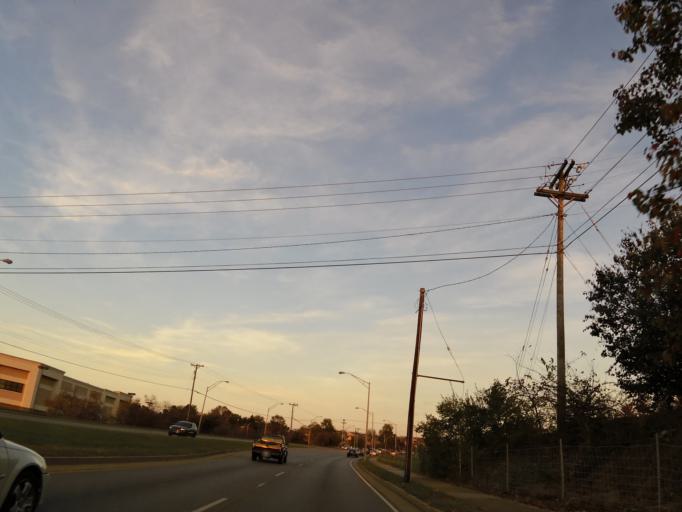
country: US
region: Kentucky
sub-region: Fayette County
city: Lexington
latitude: 37.9688
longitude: -84.4996
